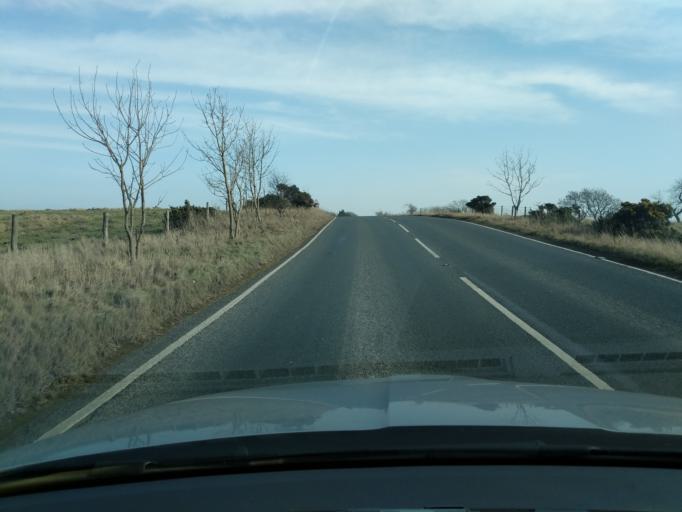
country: GB
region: England
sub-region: North Yorkshire
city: Catterick Garrison
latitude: 54.3474
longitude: -1.7725
